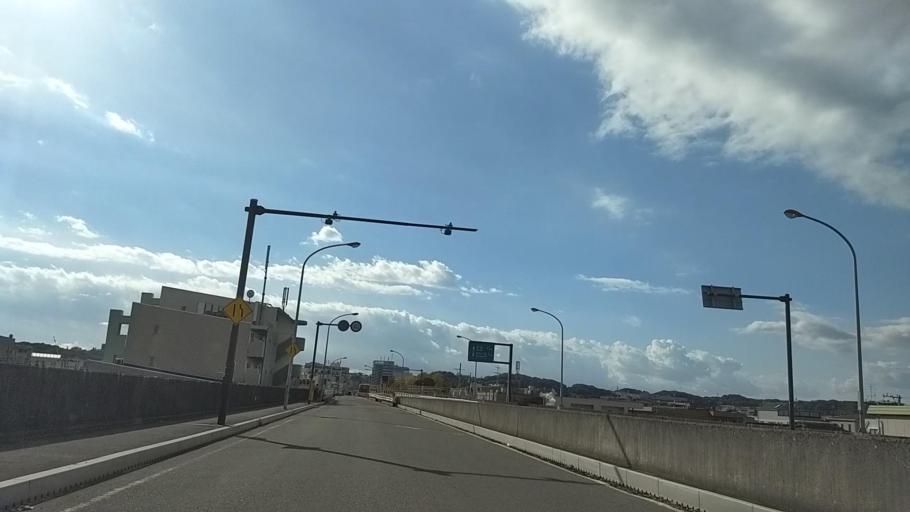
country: JP
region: Tokyo
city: Chofugaoka
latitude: 35.6239
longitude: 139.5672
